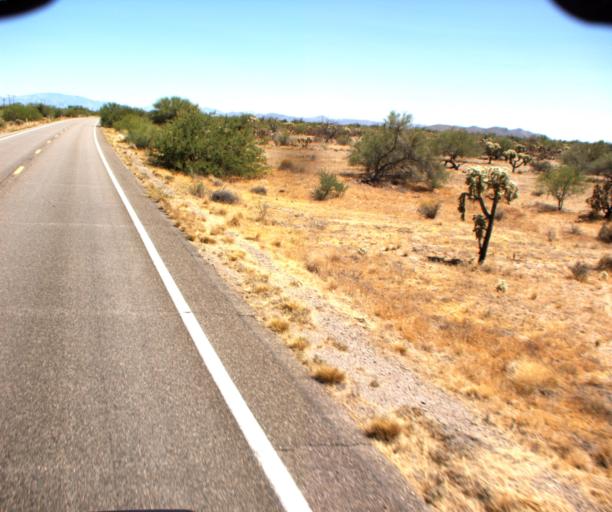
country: US
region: Arizona
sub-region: Pima County
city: Catalina
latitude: 32.7483
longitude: -111.1308
